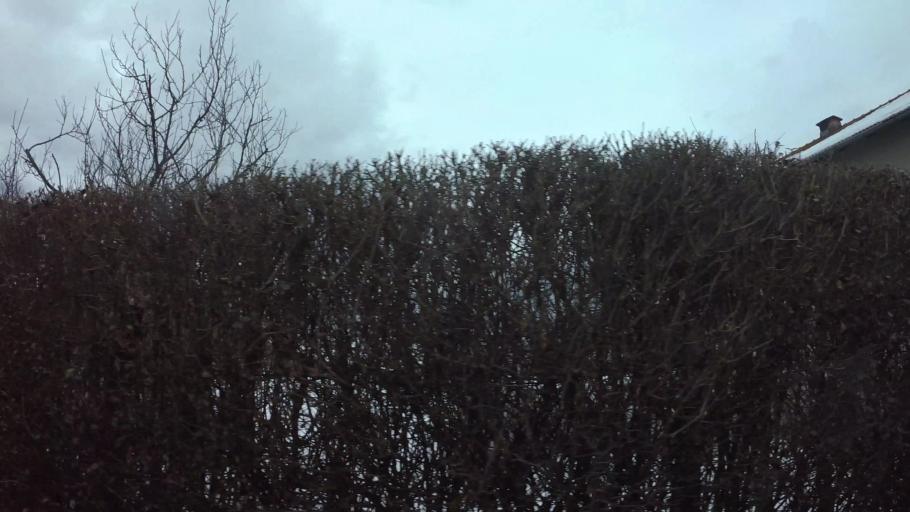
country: BA
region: Federation of Bosnia and Herzegovina
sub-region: Kanton Sarajevo
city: Sarajevo
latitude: 43.8679
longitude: 18.3202
